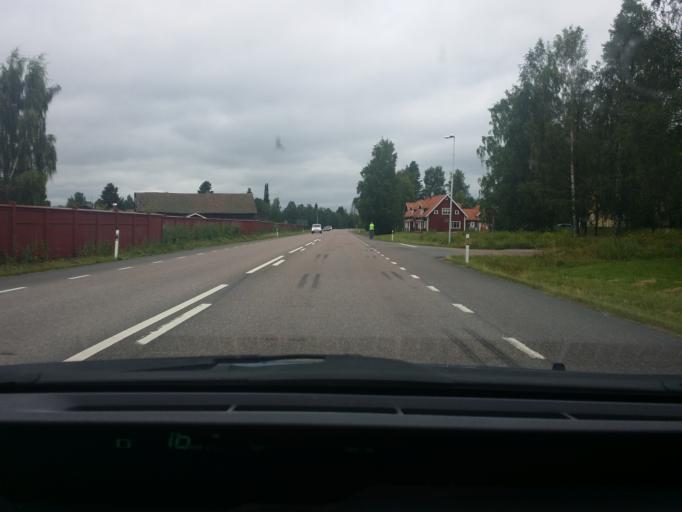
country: SE
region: Dalarna
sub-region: Gagnefs Kommun
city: Djuras
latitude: 60.5632
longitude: 15.1301
